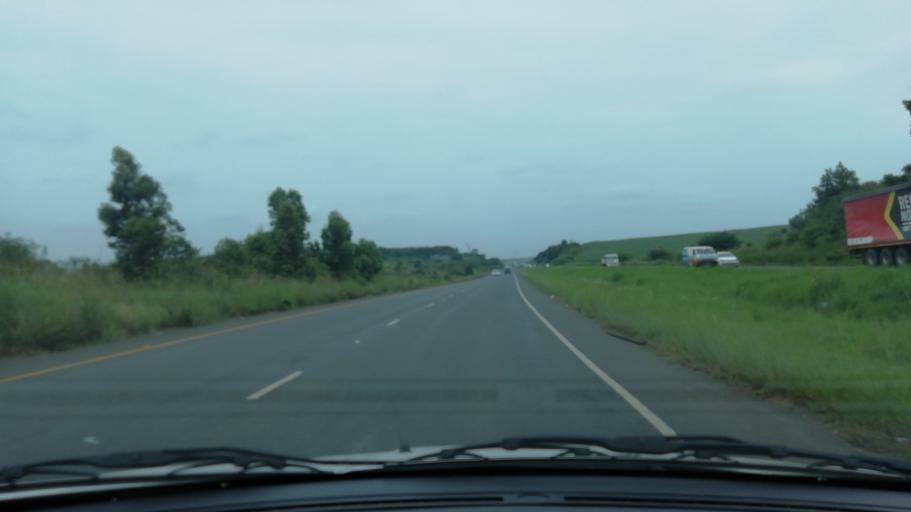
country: ZA
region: KwaZulu-Natal
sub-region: uThungulu District Municipality
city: Empangeni
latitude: -28.7669
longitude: 31.9222
